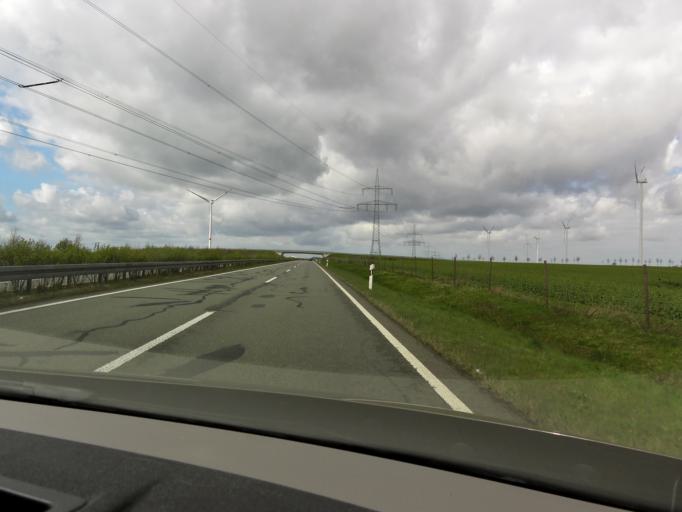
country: DE
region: Mecklenburg-Vorpommern
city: Brandshagen
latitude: 54.1822
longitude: 13.1687
